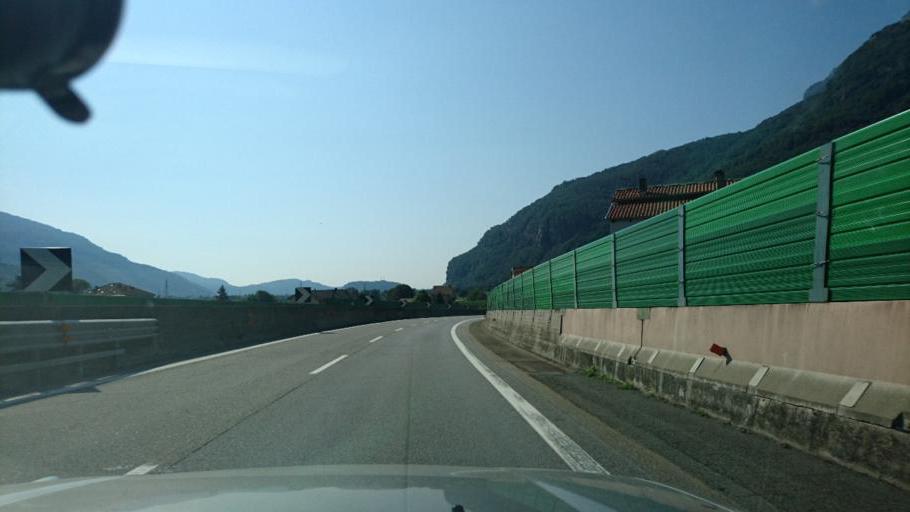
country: IT
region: Piedmont
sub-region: Provincia di Torino
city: Tavagnasco
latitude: 45.5475
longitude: 7.8235
